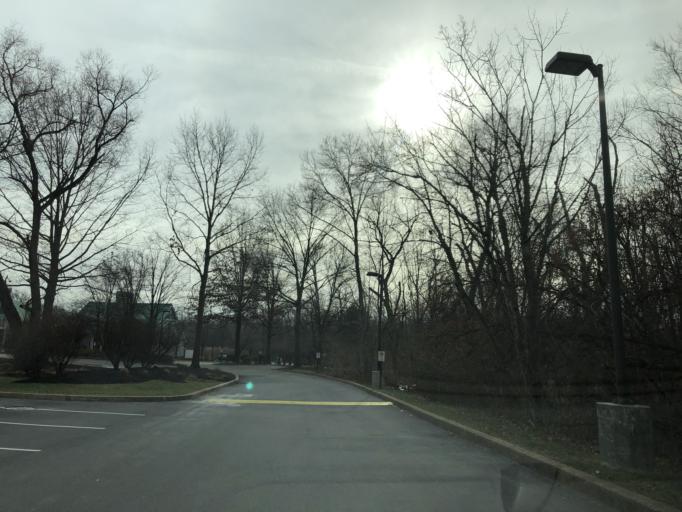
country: US
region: Pennsylvania
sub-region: Chester County
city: Exton
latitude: 40.0268
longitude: -75.6415
